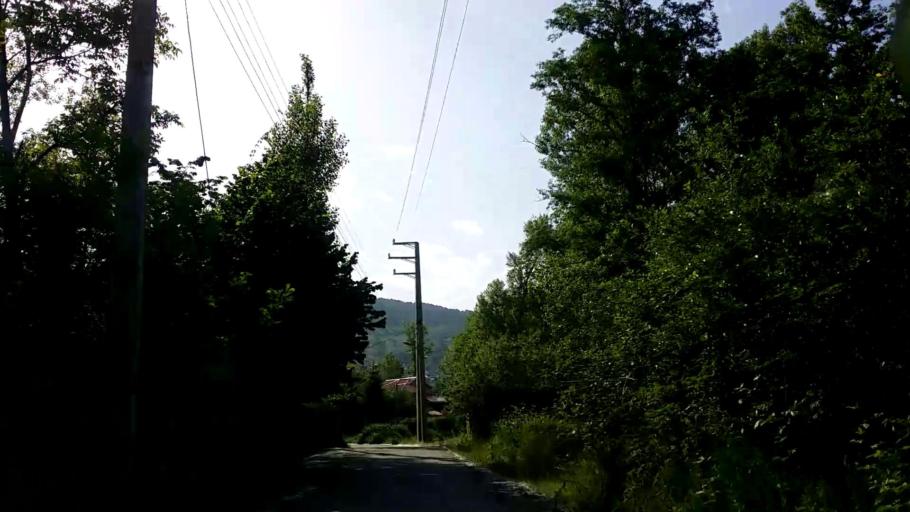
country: IR
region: Mazandaran
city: `Abbasabad
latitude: 36.5225
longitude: 51.1764
